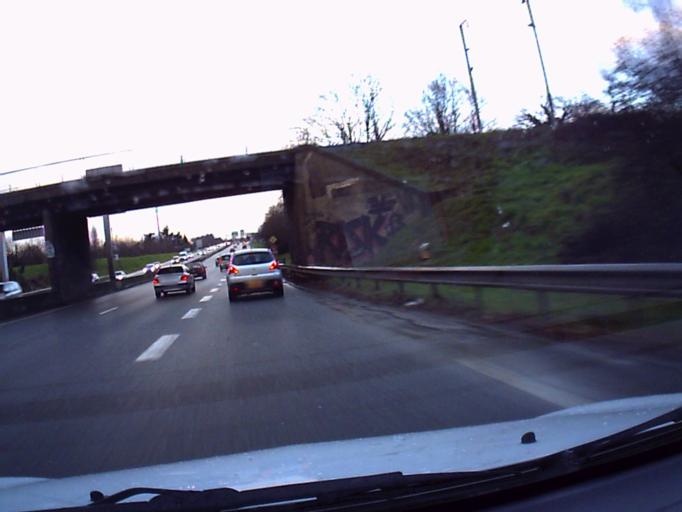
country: FR
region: Brittany
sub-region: Departement d'Ille-et-Vilaine
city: Vezin-le-Coquet
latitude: 48.1117
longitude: -1.7183
